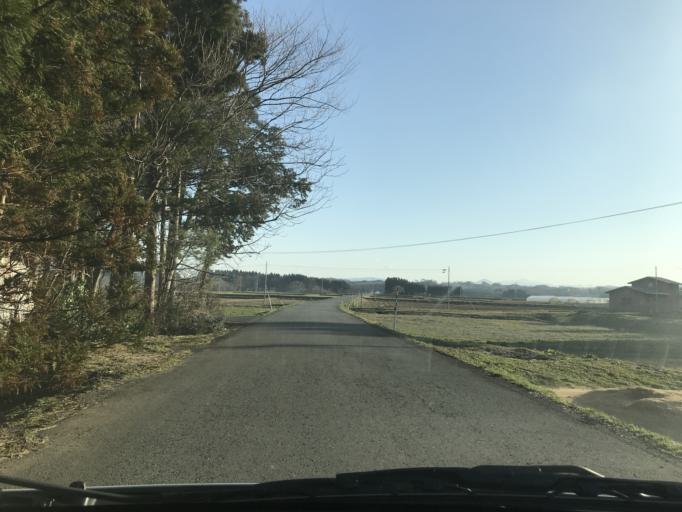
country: JP
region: Iwate
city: Kitakami
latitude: 39.2202
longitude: 141.0410
